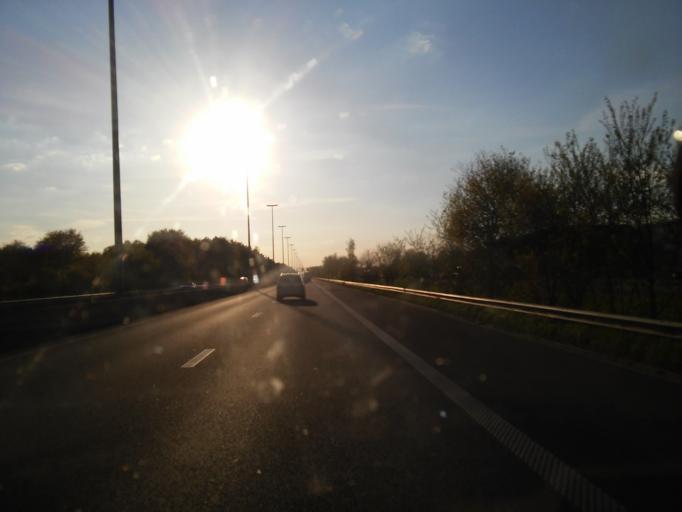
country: BE
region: Flanders
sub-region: Provincie Antwerpen
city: Olen
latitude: 51.1444
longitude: 4.8920
